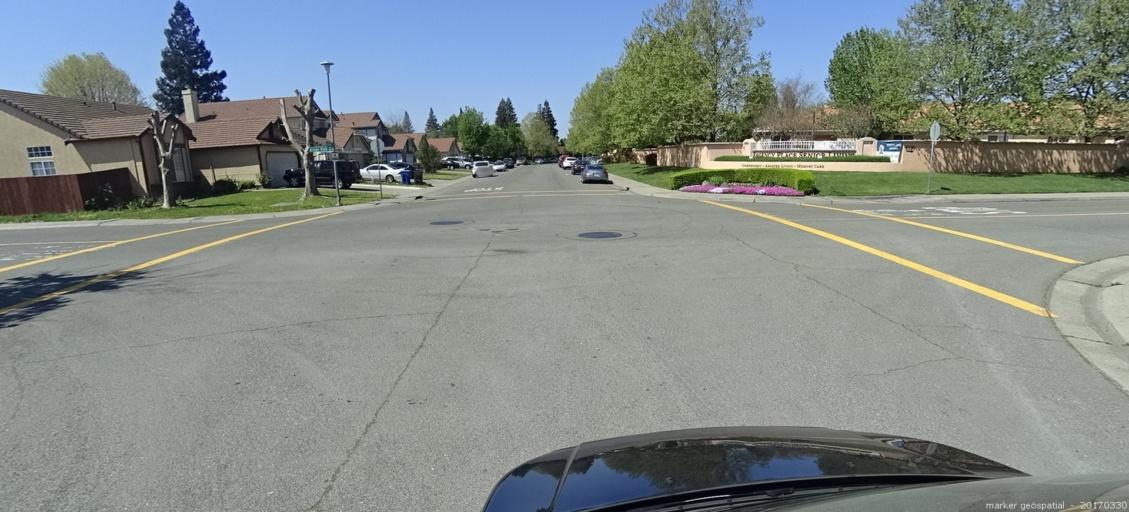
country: US
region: California
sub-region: Sacramento County
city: Florin
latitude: 38.4618
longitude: -121.4212
